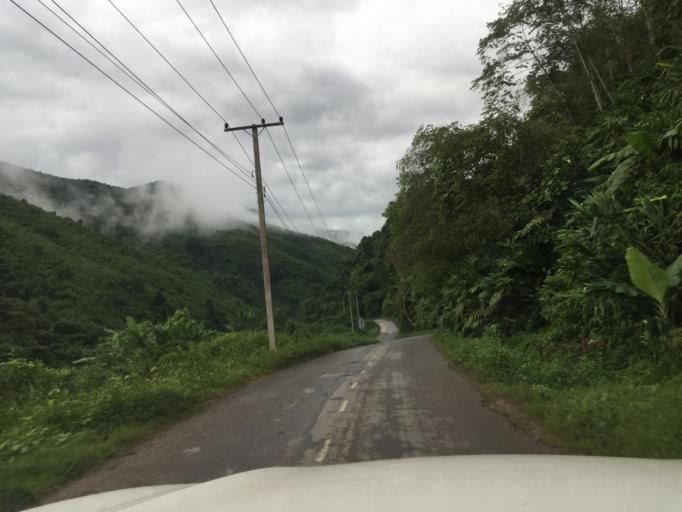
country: LA
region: Oudomxai
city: Muang La
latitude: 21.0460
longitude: 102.2410
